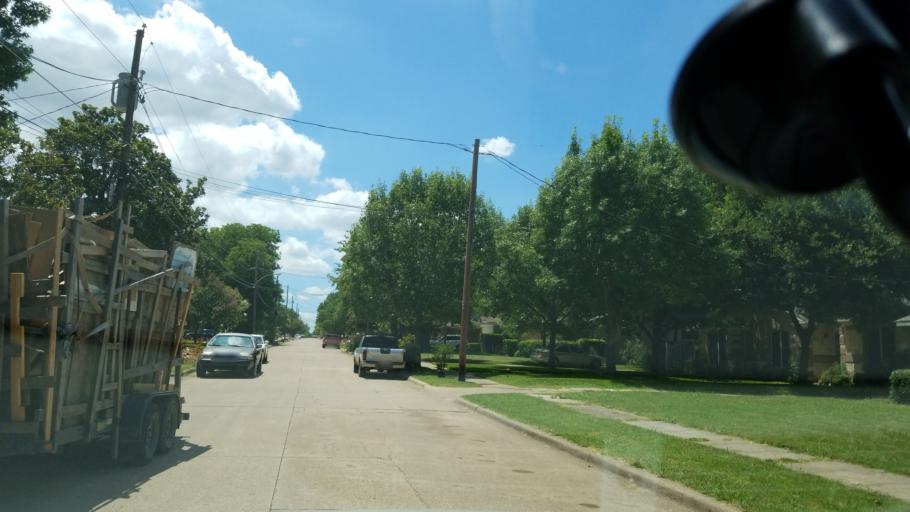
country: US
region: Texas
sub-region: Dallas County
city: Cockrell Hill
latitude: 32.6970
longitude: -96.8665
